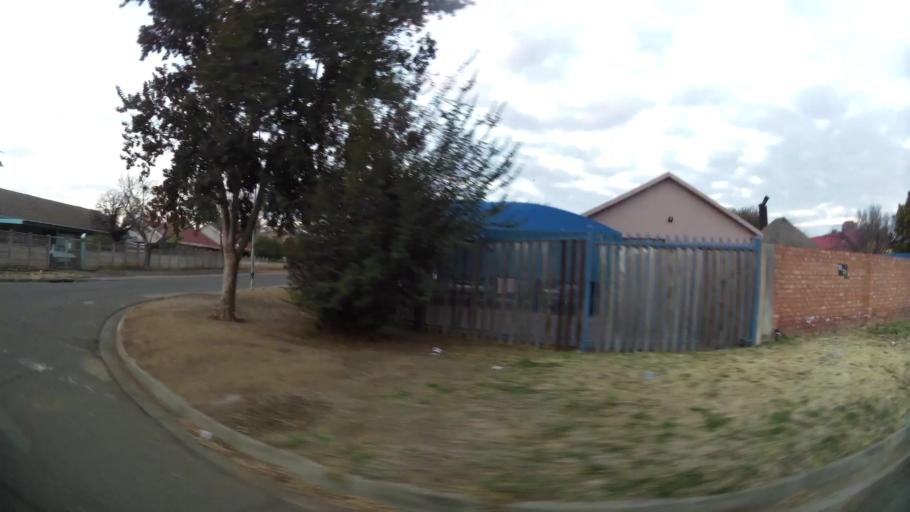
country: ZA
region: Orange Free State
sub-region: Mangaung Metropolitan Municipality
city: Bloemfontein
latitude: -29.1681
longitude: 26.1851
